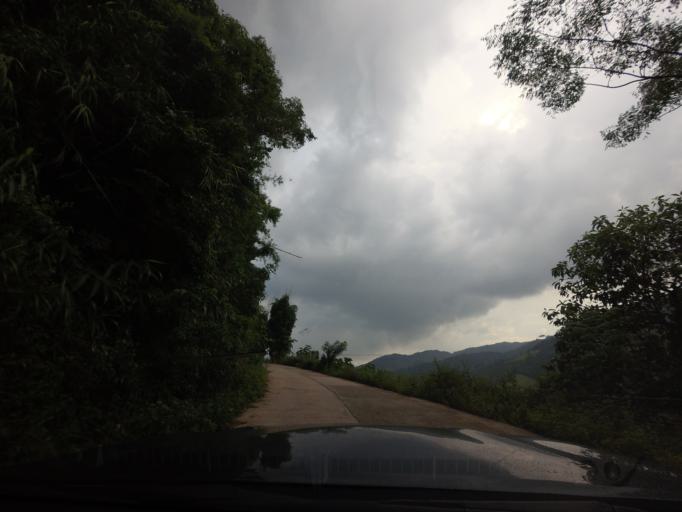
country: TH
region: Nan
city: Bo Kluea
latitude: 19.3511
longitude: 101.1621
